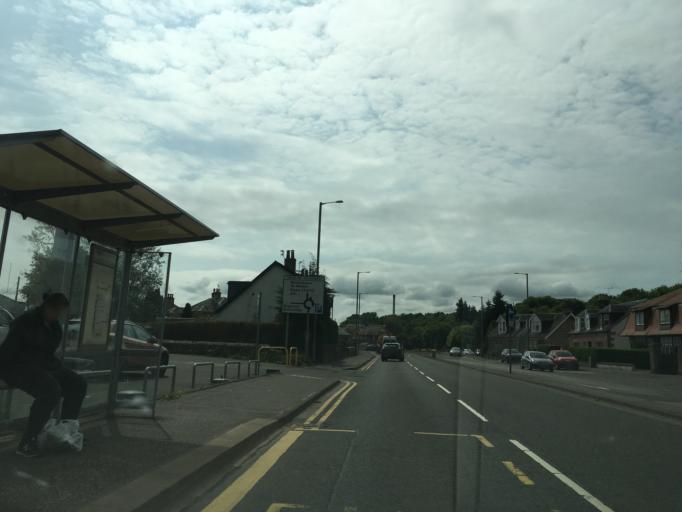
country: GB
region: Scotland
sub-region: Stirling
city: Stirling
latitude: 56.1135
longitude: -3.9325
